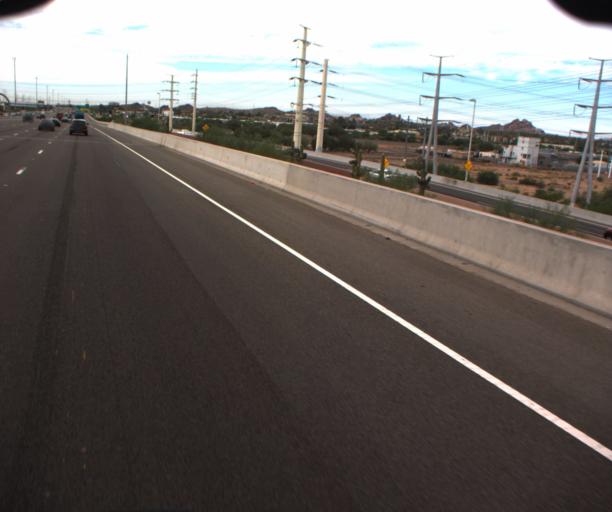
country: US
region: Arizona
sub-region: Maricopa County
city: Tempe
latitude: 33.4362
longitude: -111.9109
